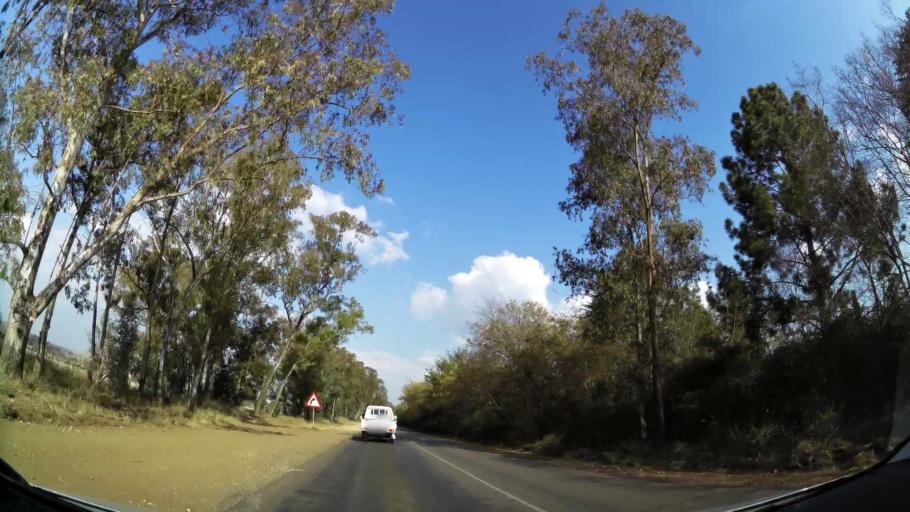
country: ZA
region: Gauteng
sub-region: Ekurhuleni Metropolitan Municipality
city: Tembisa
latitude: -25.9291
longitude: 28.2313
